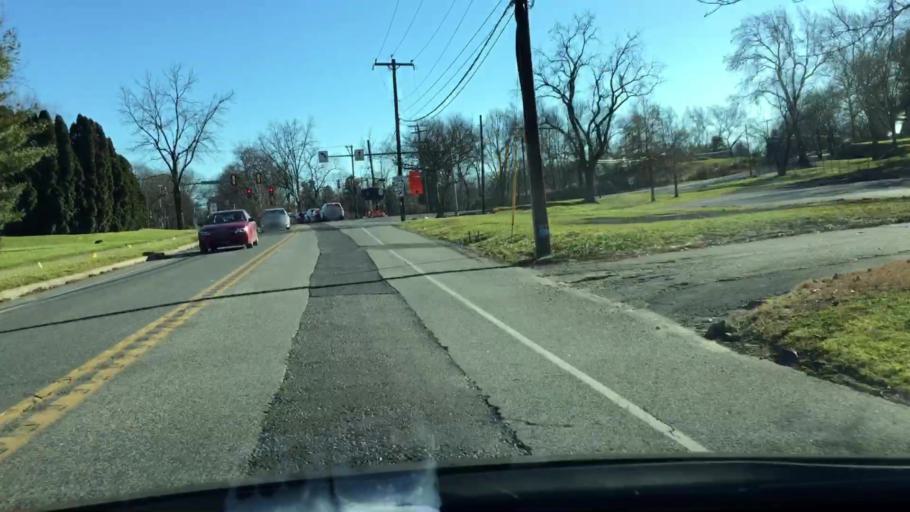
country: US
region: Pennsylvania
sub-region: Montgomery County
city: Oreland
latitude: 40.1265
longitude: -75.1660
